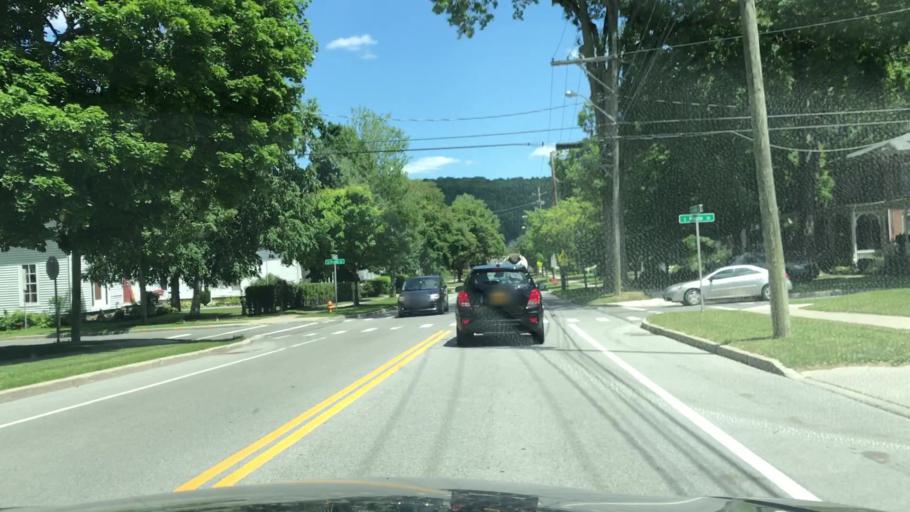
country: US
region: New York
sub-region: Wyoming County
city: Warsaw
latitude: 42.7404
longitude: -78.1396
